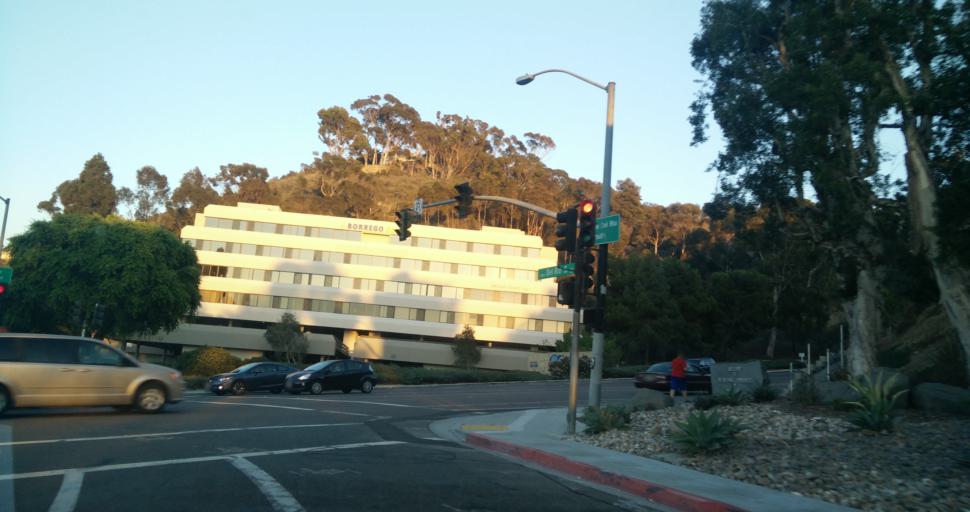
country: US
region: California
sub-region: San Diego County
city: San Diego
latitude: 32.7673
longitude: -117.1396
